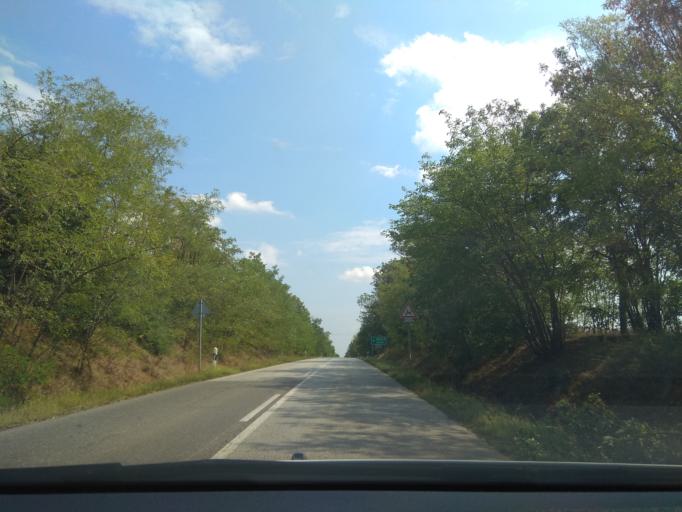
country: HU
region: Heves
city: Szihalom
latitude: 47.8222
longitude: 20.4889
